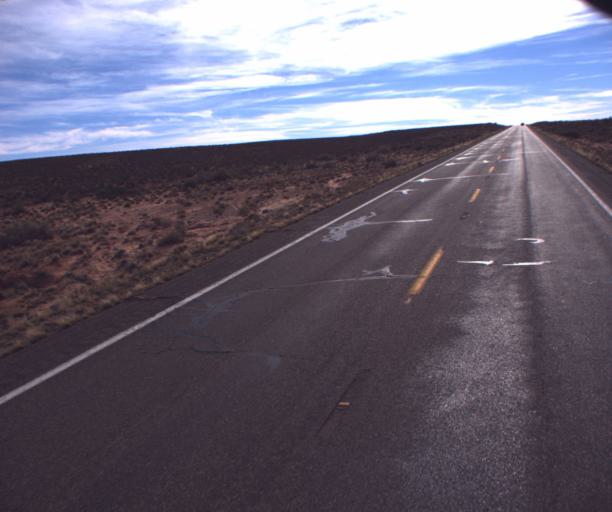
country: US
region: Arizona
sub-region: Coconino County
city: LeChee
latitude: 36.8348
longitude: -111.3184
